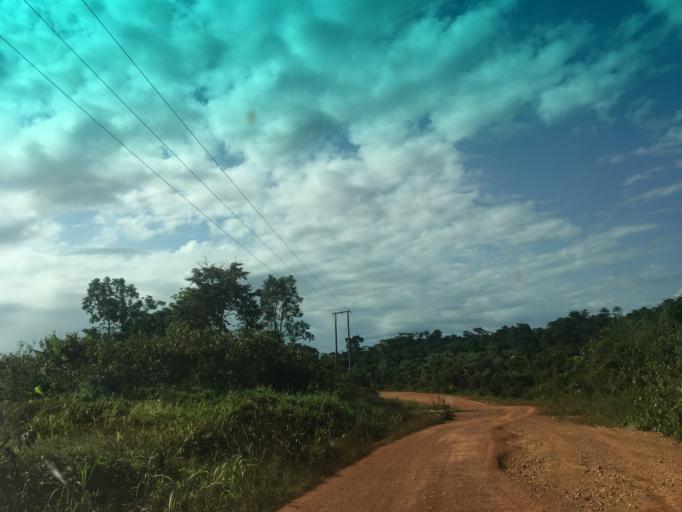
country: GH
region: Western
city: Wassa-Akropong
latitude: 5.9158
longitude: -2.4058
